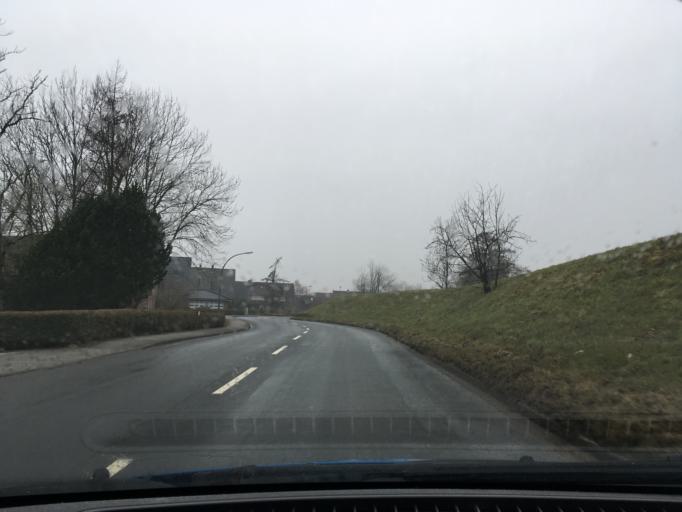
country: DE
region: Lower Saxony
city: Neu Wulmstorf
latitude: 53.5103
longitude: 9.8320
